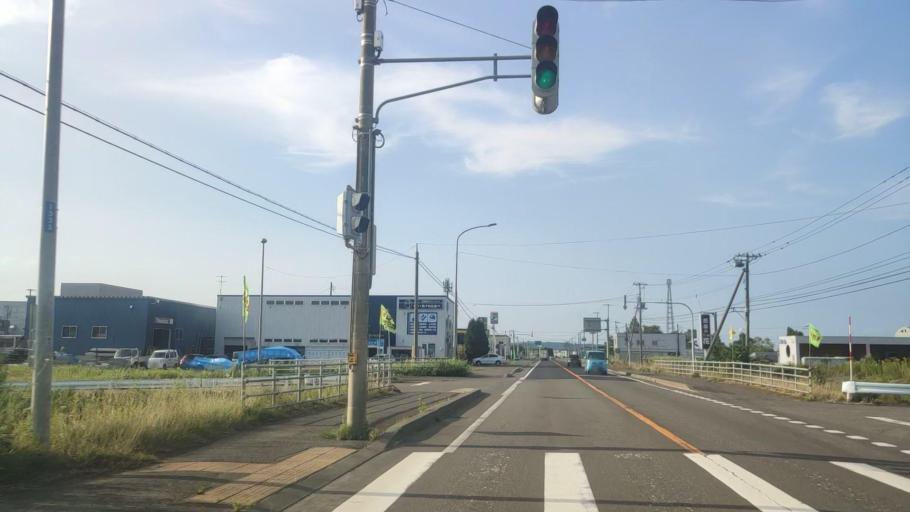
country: JP
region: Hokkaido
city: Iwamizawa
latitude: 43.0104
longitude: 141.7891
